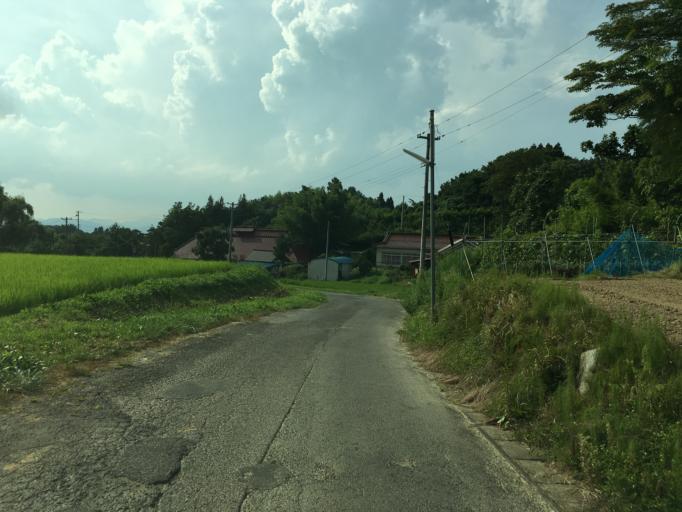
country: JP
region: Fukushima
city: Miharu
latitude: 37.4177
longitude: 140.4488
